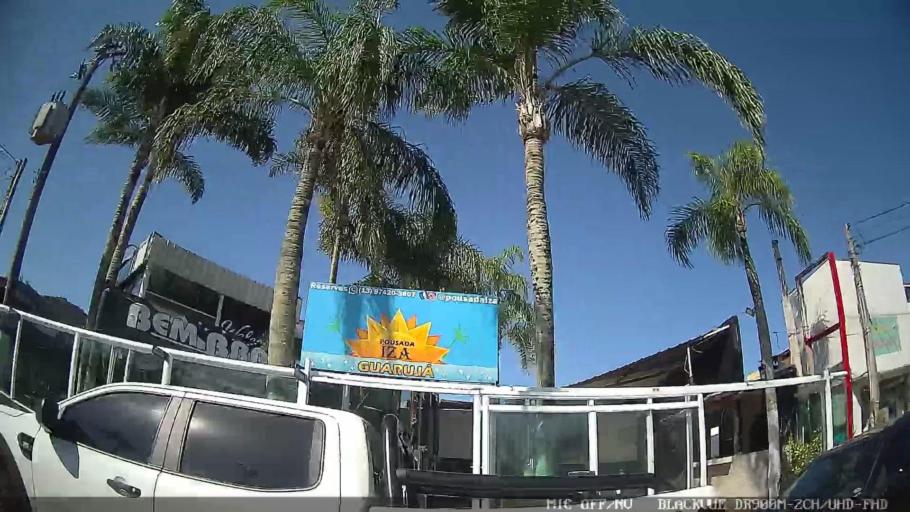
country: BR
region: Sao Paulo
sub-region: Guaruja
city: Guaruja
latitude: -23.9875
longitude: -46.2043
